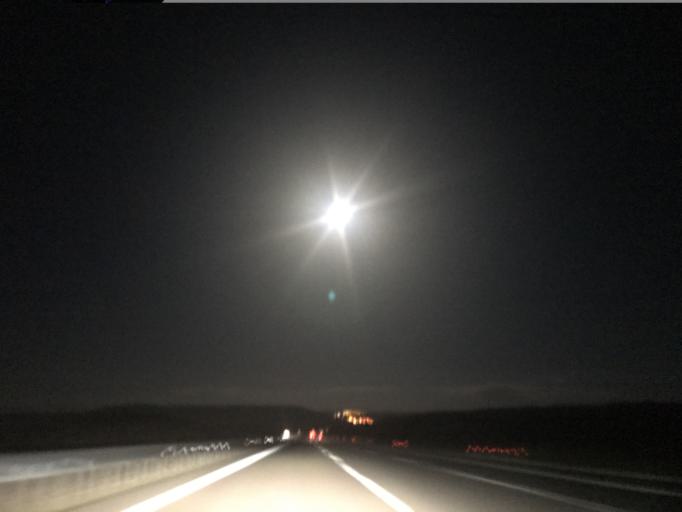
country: TR
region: Nigde
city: Ulukisla
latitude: 37.6351
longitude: 34.4244
